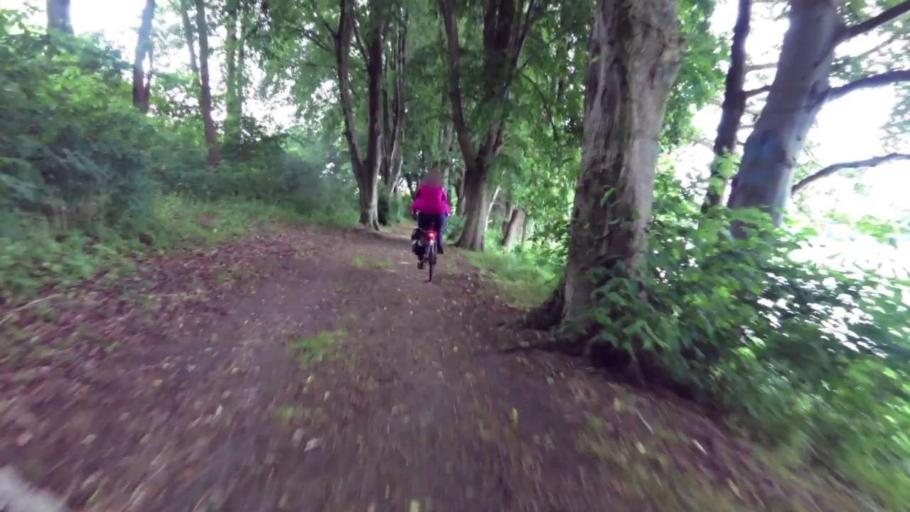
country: PL
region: West Pomeranian Voivodeship
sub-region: Powiat stargardzki
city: Chociwel
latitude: 53.4668
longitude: 15.3504
